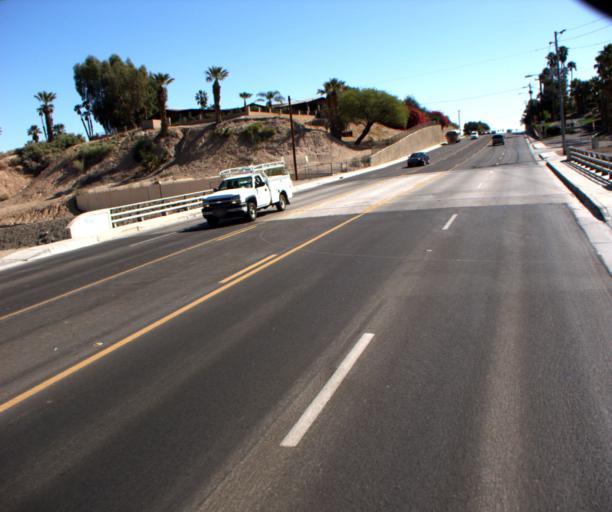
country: US
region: Arizona
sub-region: Yuma County
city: Yuma
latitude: 32.6984
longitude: -114.6419
